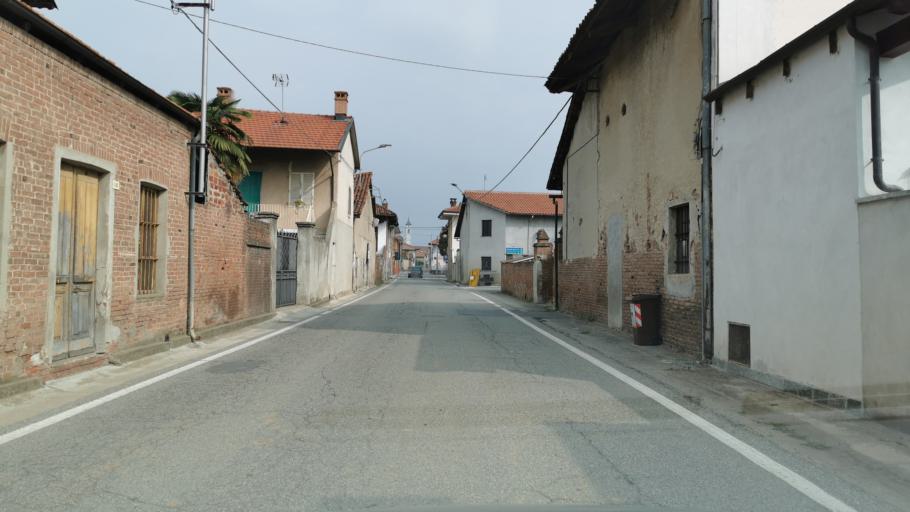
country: IT
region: Piedmont
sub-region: Provincia di Torino
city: Tonengo-Casale
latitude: 45.2828
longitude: 7.9356
